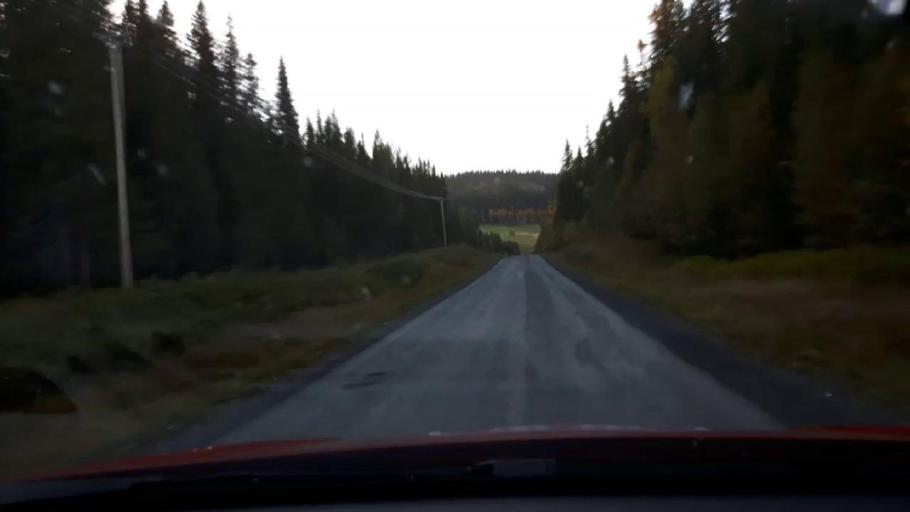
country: SE
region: Jaemtland
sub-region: Krokoms Kommun
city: Krokom
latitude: 63.4816
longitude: 14.2108
